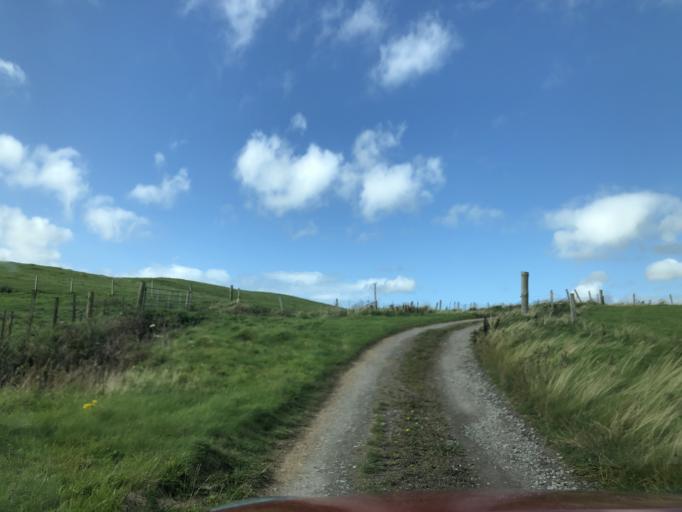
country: GB
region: Scotland
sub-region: Argyll and Bute
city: Campbeltown
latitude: 55.3094
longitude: -5.6080
